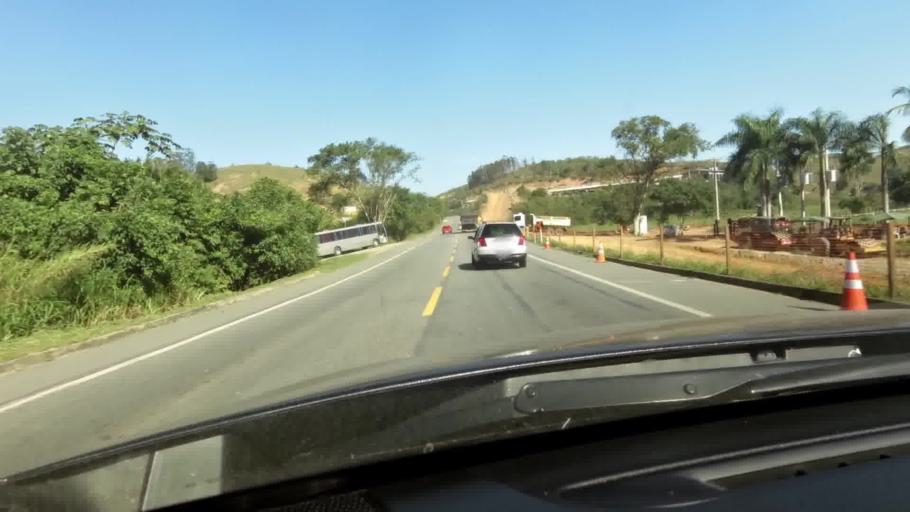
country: BR
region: Espirito Santo
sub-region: Rio Novo Do Sul
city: Rio Novo do Sul
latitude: -20.8945
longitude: -41.0053
